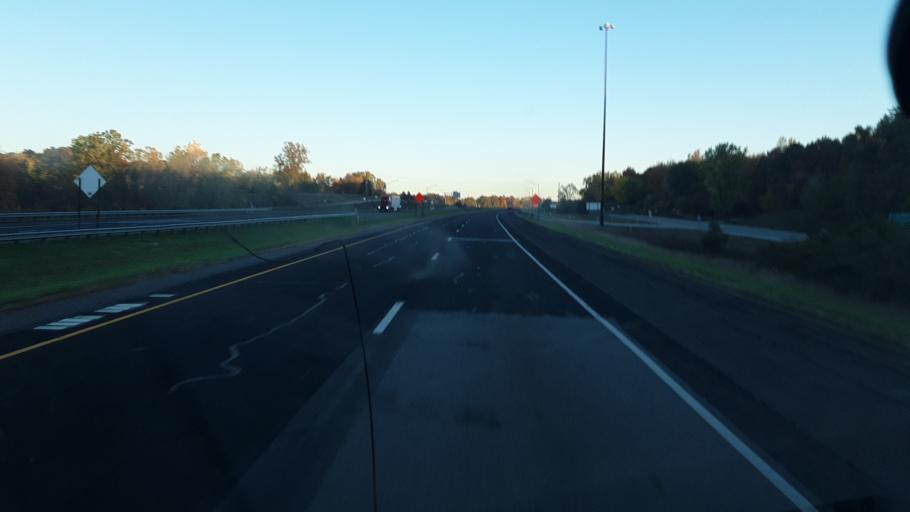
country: US
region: Indiana
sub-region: Steuben County
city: Angola
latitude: 41.7064
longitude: -85.0046
